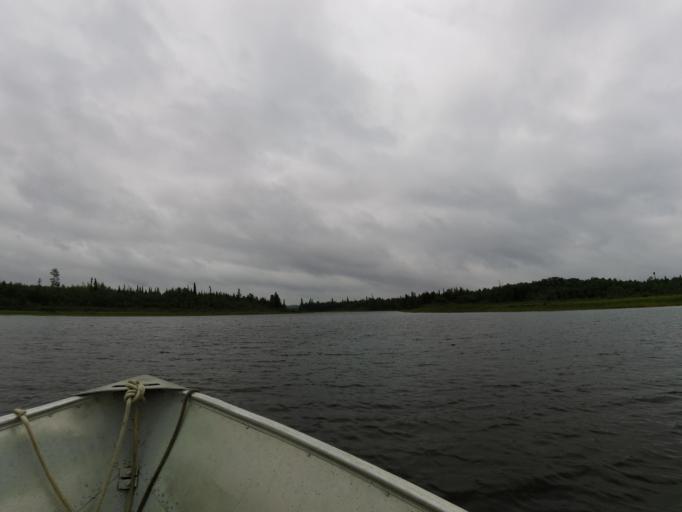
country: CA
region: Ontario
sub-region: Rainy River District
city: Atikokan
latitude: 49.5979
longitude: -91.3420
